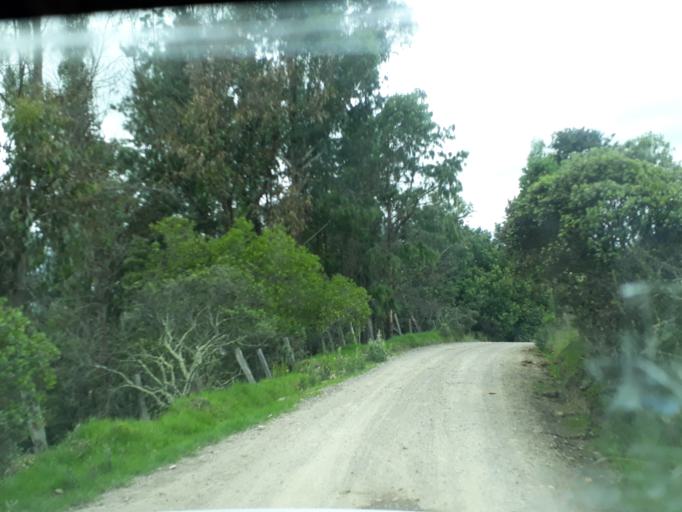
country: CO
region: Cundinamarca
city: La Mesa
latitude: 5.2695
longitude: -73.9000
